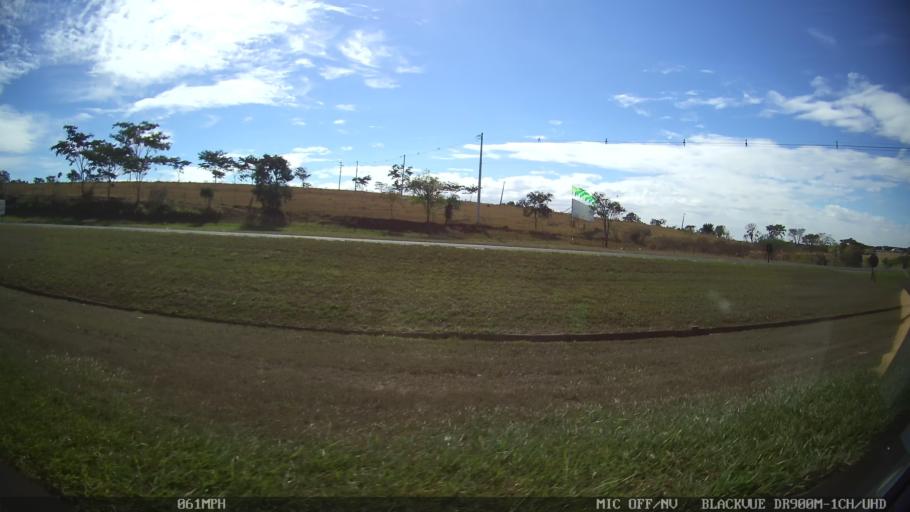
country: BR
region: Sao Paulo
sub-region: Sao Jose Do Rio Preto
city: Sao Jose do Rio Preto
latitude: -20.8149
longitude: -49.4686
